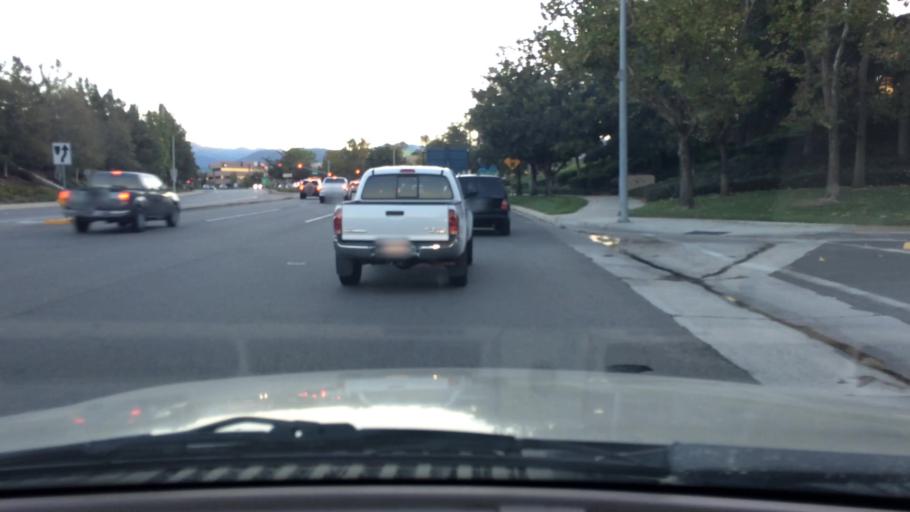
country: US
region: California
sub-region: Orange County
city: Rancho Santa Margarita
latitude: 33.6375
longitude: -117.6107
